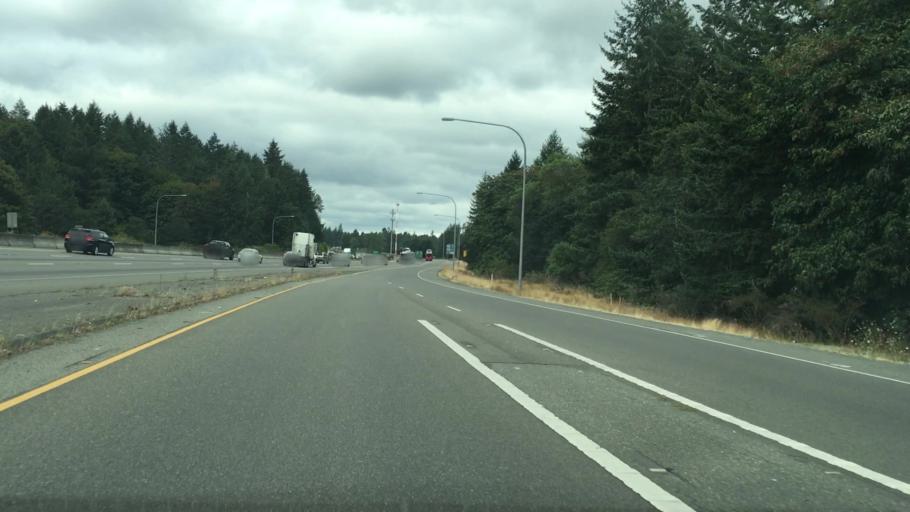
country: US
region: Washington
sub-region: Pierce County
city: Fort Lewis
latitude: 47.1034
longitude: -122.5926
